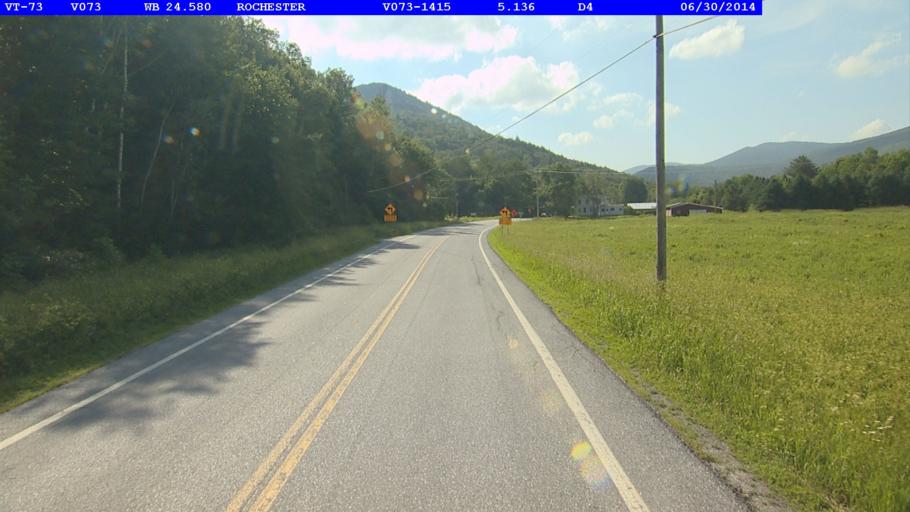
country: US
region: Vermont
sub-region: Orange County
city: Randolph
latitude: 43.8573
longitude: -72.8688
